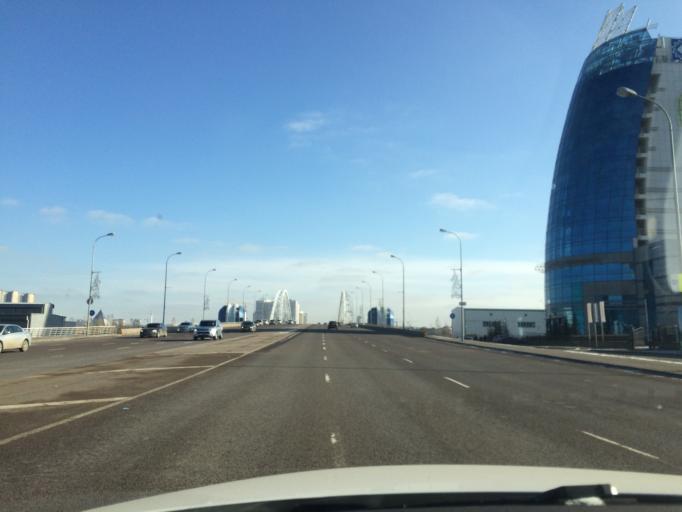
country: KZ
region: Astana Qalasy
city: Astana
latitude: 51.1215
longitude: 71.4396
